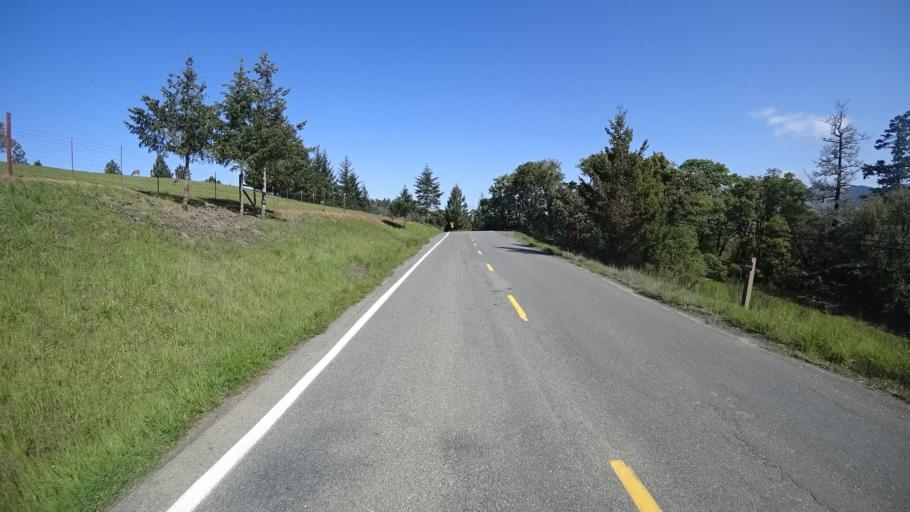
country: US
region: California
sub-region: Humboldt County
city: Redway
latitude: 40.1104
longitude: -123.7527
